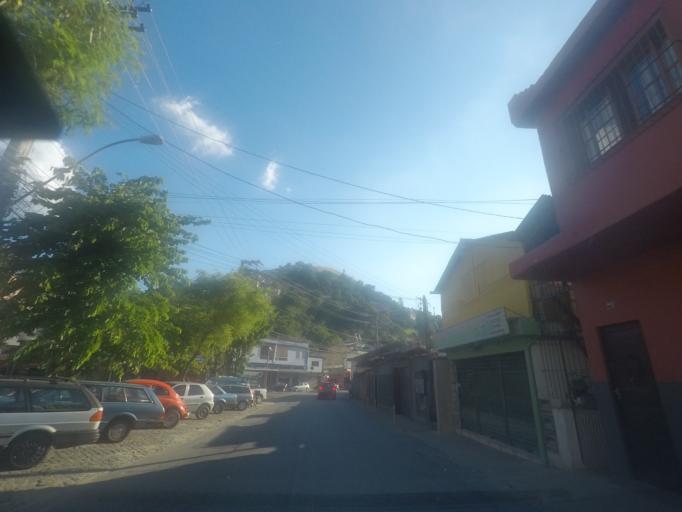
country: BR
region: Rio de Janeiro
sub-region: Petropolis
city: Petropolis
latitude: -22.4885
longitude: -43.1526
